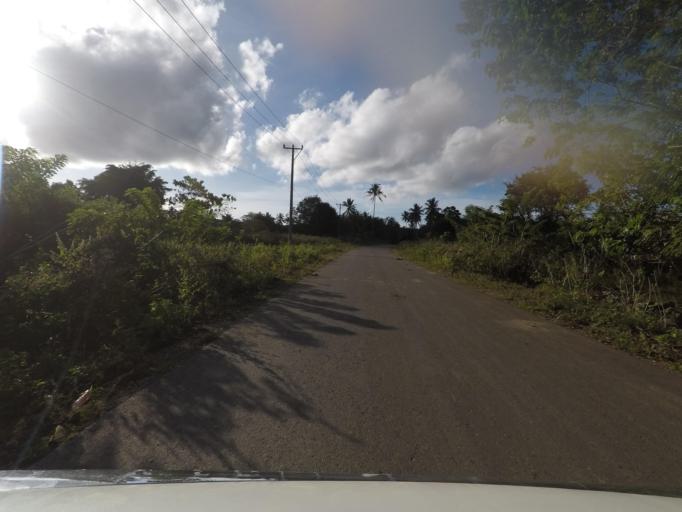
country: TL
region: Lautem
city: Lospalos
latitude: -8.4328
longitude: 127.0041
